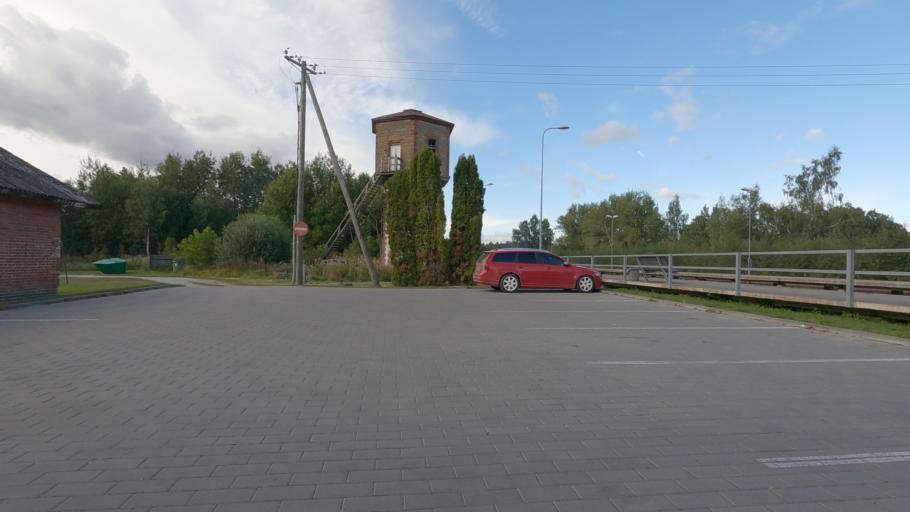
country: EE
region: Raplamaa
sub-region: Rapla vald
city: Rapla
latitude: 58.9940
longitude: 24.8320
